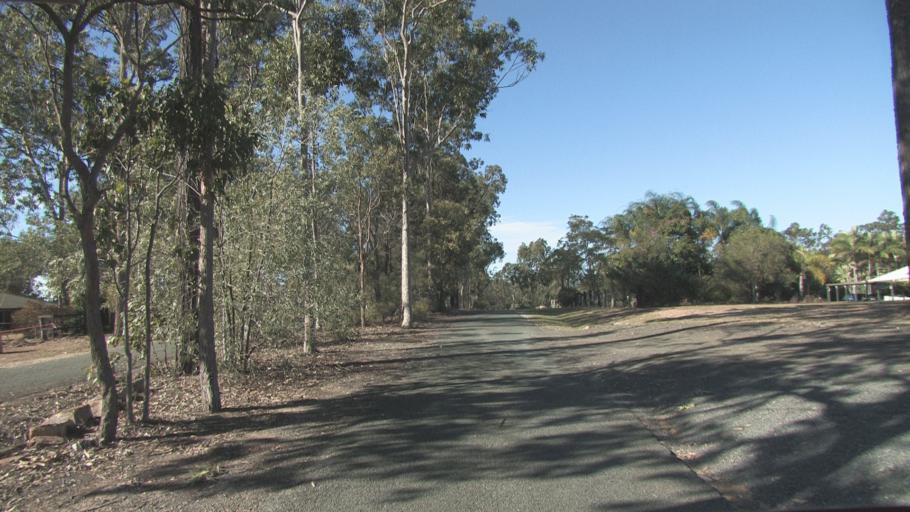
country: AU
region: Queensland
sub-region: Ipswich
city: Springfield Lakes
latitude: -27.7345
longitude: 152.9254
